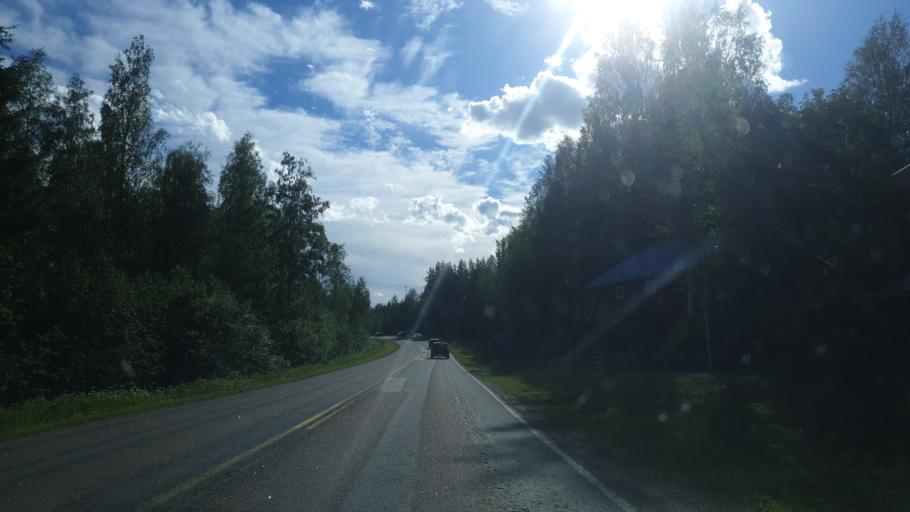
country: FI
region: Southern Savonia
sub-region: Mikkeli
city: Pertunmaa
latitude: 61.5188
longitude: 26.4936
